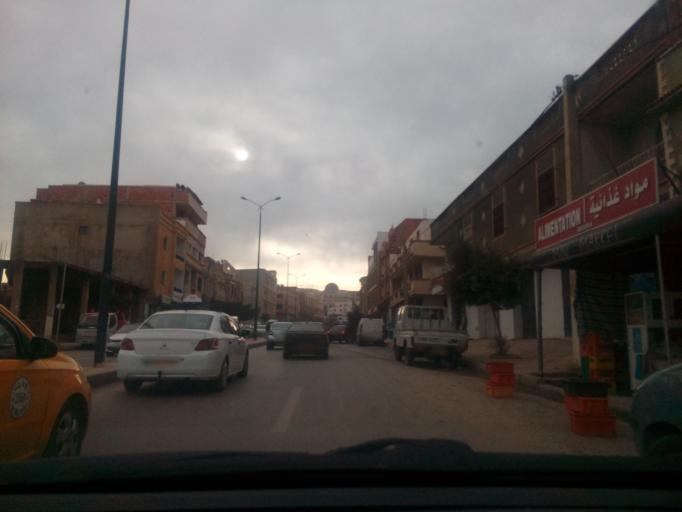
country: DZ
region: Tlemcen
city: Mansoura
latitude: 34.8823
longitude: -1.3503
